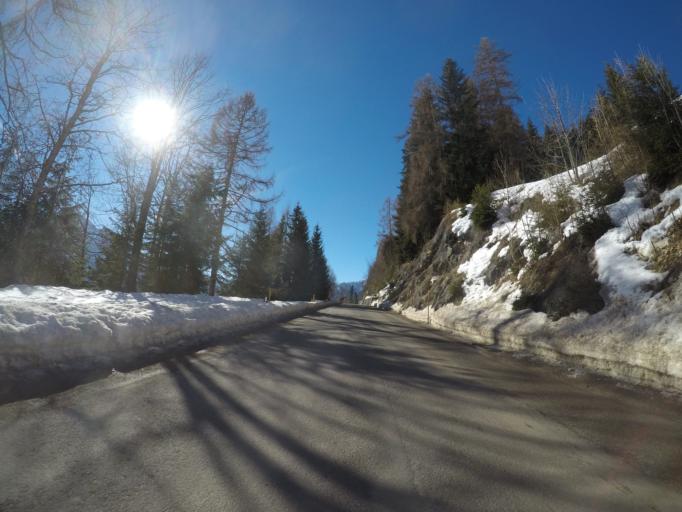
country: IT
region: Veneto
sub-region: Provincia di Belluno
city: Colle Santa Lucia
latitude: 46.4461
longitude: 12.0060
